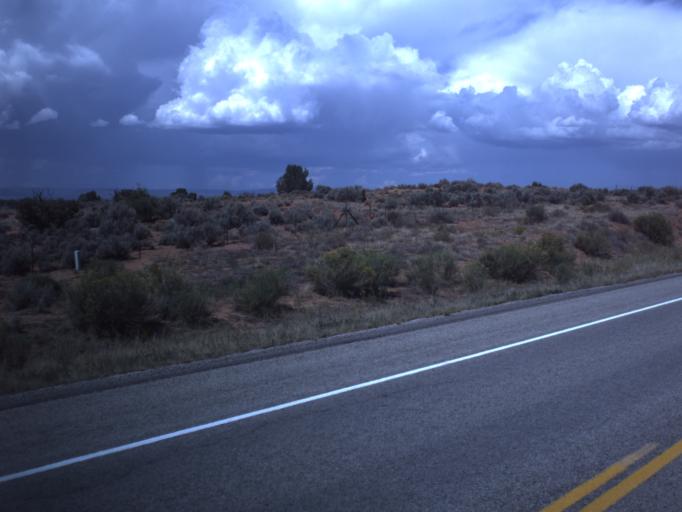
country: US
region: Utah
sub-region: San Juan County
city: Blanding
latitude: 37.4733
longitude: -109.4670
